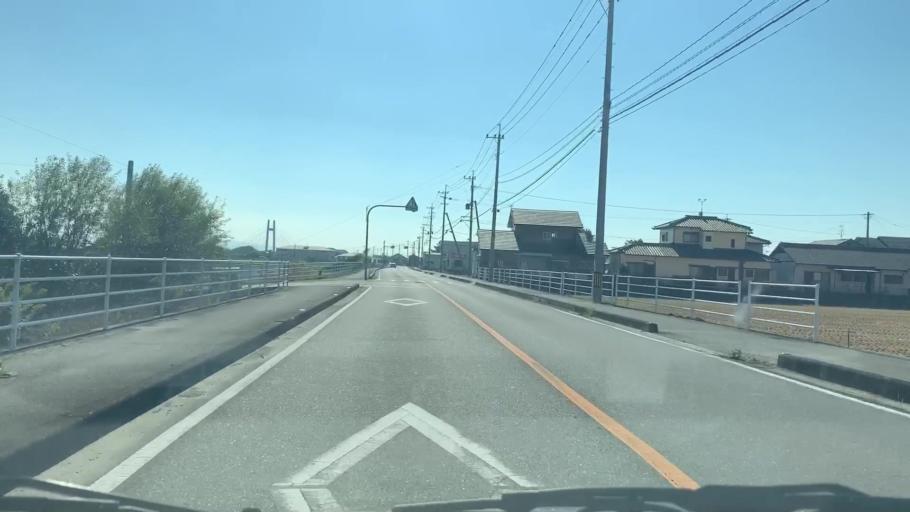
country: JP
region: Saga Prefecture
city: Kanzakimachi-kanzaki
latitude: 33.2942
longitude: 130.4449
